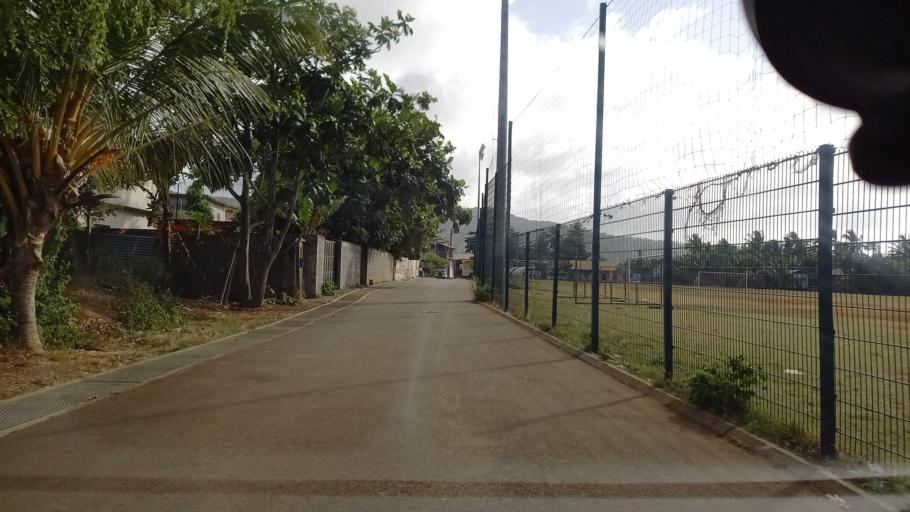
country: YT
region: Bandrele
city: Bandrele
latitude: -12.9119
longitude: 45.1955
